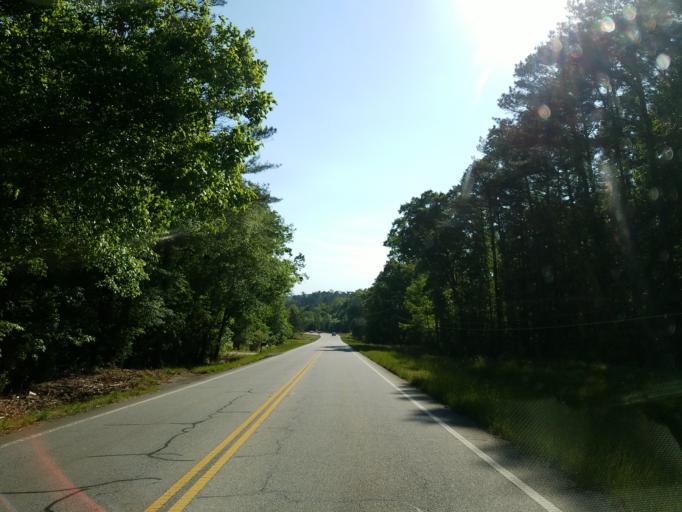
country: US
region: Georgia
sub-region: Paulding County
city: Dallas
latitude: 33.9091
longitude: -84.8687
